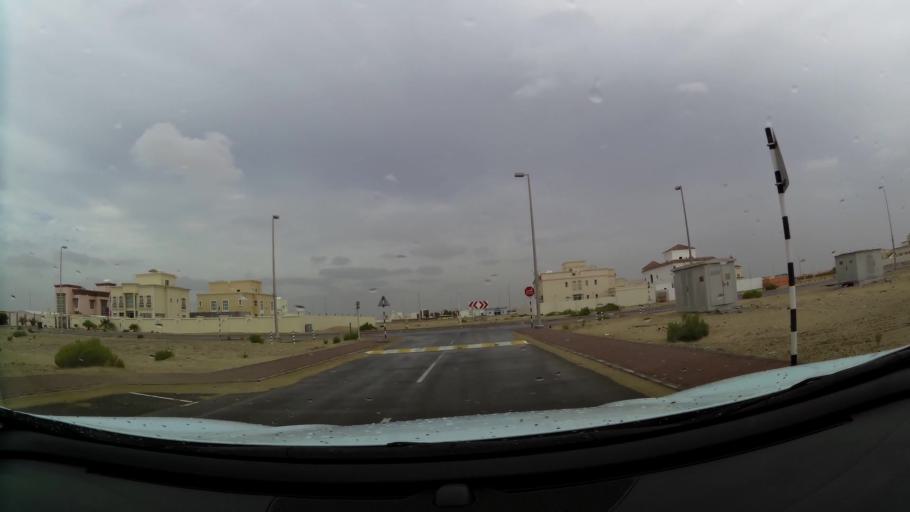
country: AE
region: Abu Dhabi
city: Abu Dhabi
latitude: 24.3659
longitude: 54.6227
